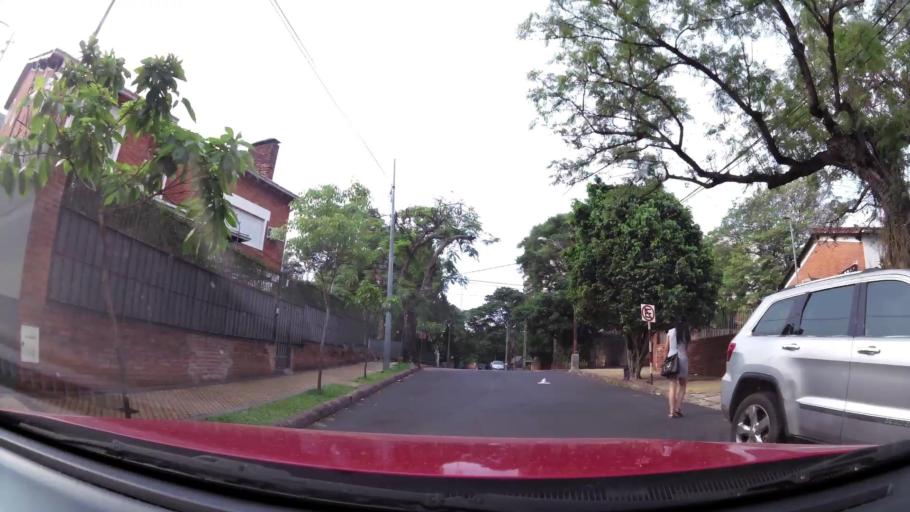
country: PY
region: Asuncion
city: Asuncion
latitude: -25.2926
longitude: -57.6129
